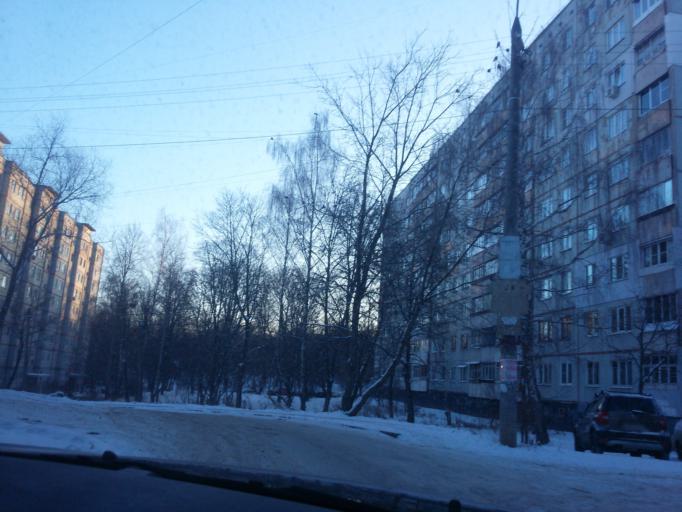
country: RU
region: Tula
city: Mendeleyevskiy
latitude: 54.1600
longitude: 37.5935
